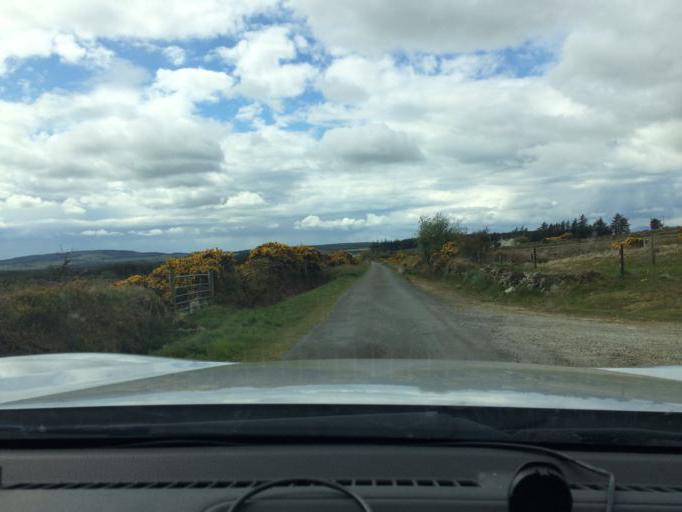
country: IE
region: Munster
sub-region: Waterford
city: Dungarvan
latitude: 52.0396
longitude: -7.6298
